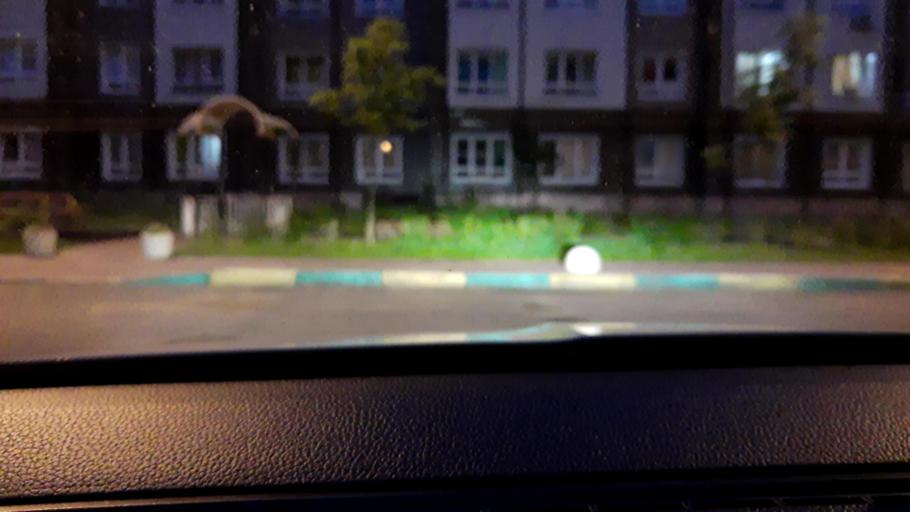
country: RU
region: Moskovskaya
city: Lesnyye Polyany
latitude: 55.9198
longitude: 37.8835
